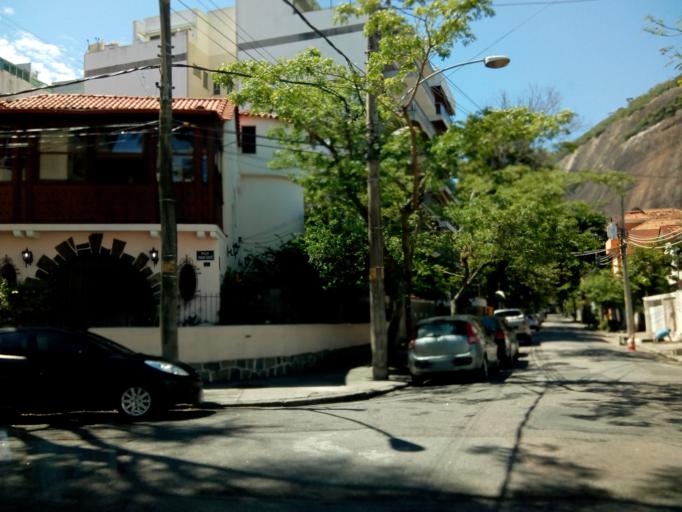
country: BR
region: Rio de Janeiro
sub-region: Rio De Janeiro
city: Rio de Janeiro
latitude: -22.9522
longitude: -43.1685
